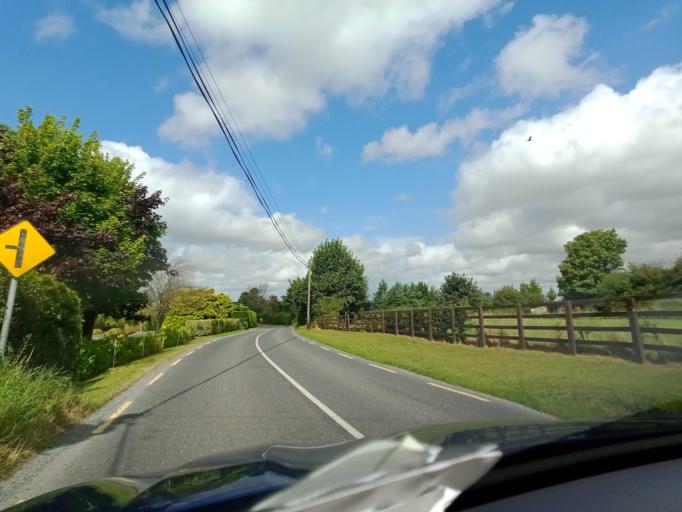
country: IE
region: Leinster
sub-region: Laois
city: Portlaoise
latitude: 53.0085
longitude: -7.2758
